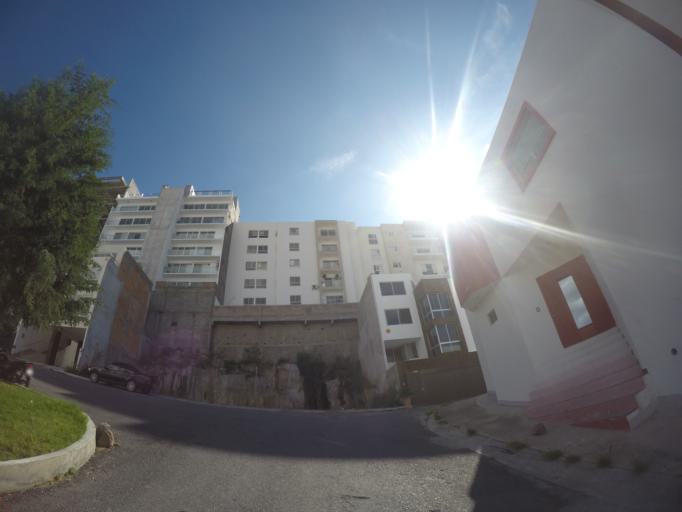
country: MX
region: San Luis Potosi
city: Escalerillas
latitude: 22.1225
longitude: -101.0326
